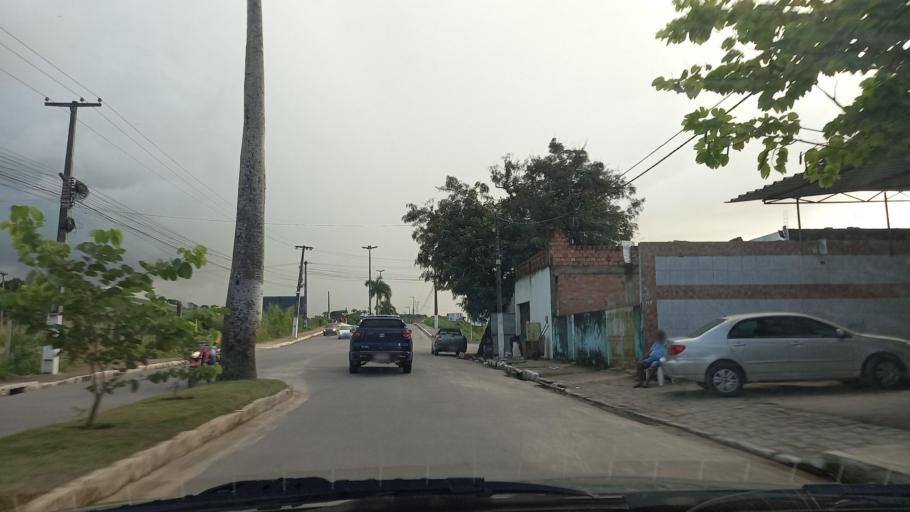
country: BR
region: Pernambuco
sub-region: Palmares
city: Palmares
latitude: -8.6879
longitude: -35.5984
